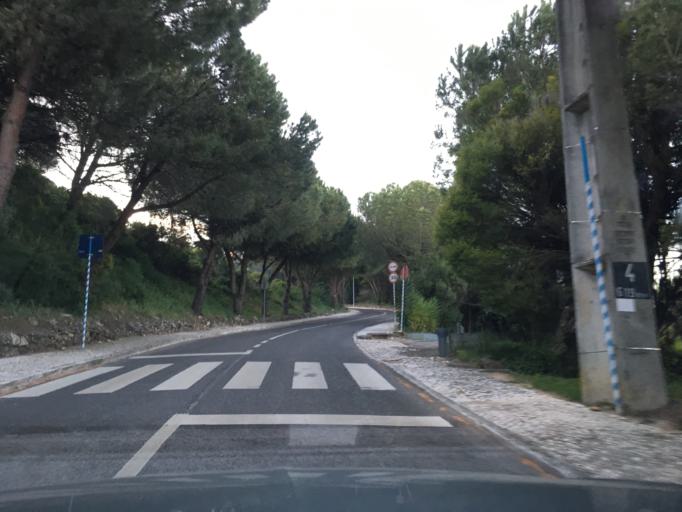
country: PT
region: Lisbon
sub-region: Oeiras
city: Quejas
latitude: 38.7181
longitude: -9.2789
